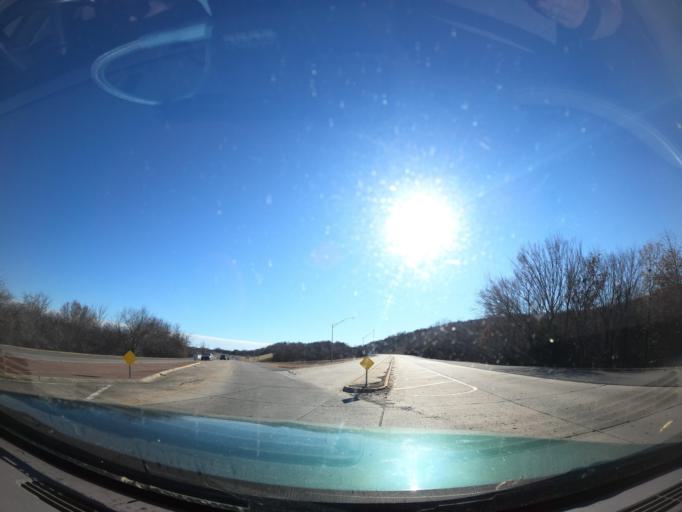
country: US
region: Oklahoma
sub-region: McIntosh County
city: Eufaula
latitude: 35.2740
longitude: -95.5858
